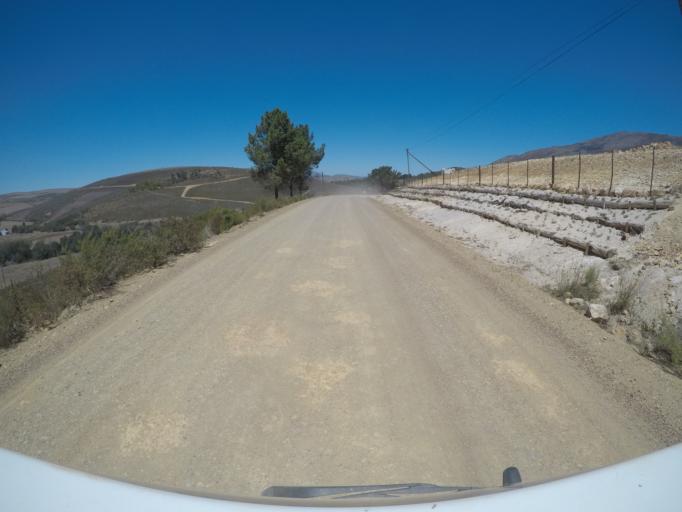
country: ZA
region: Western Cape
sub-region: Overberg District Municipality
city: Caledon
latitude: -34.1767
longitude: 19.2257
